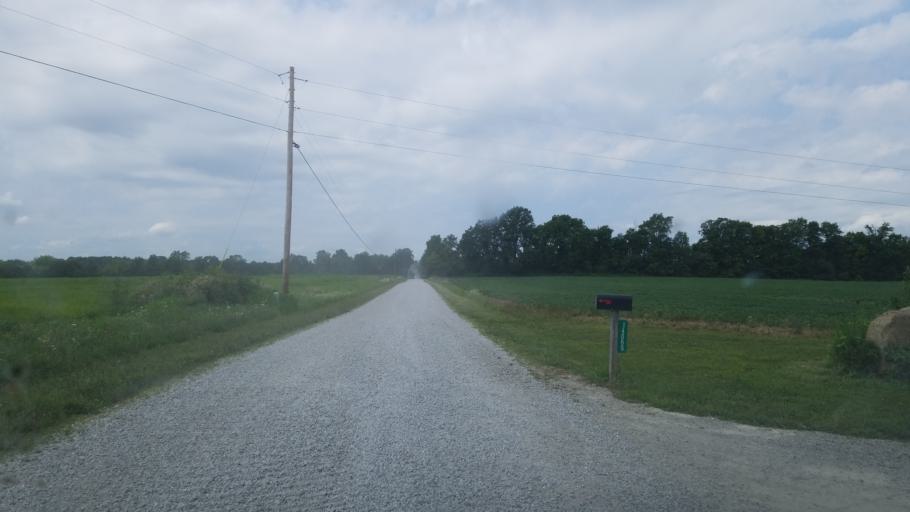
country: US
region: Ohio
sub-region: Knox County
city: Centerburg
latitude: 40.3468
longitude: -82.8014
